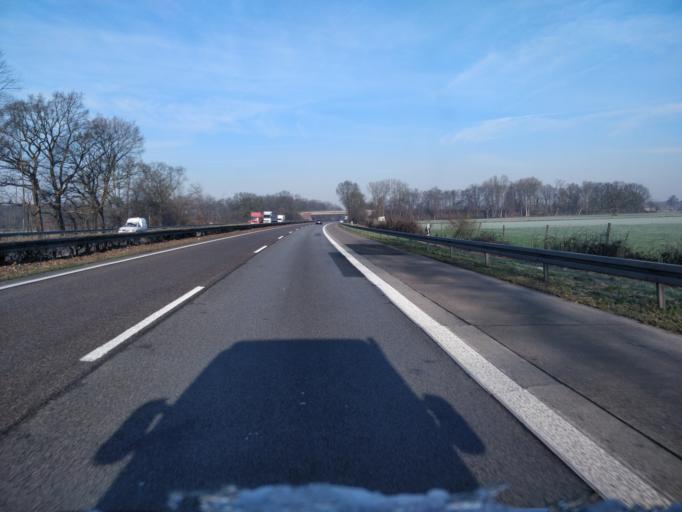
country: DE
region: North Rhine-Westphalia
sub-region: Regierungsbezirk Dusseldorf
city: Hamminkeln
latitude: 51.7132
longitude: 6.6227
